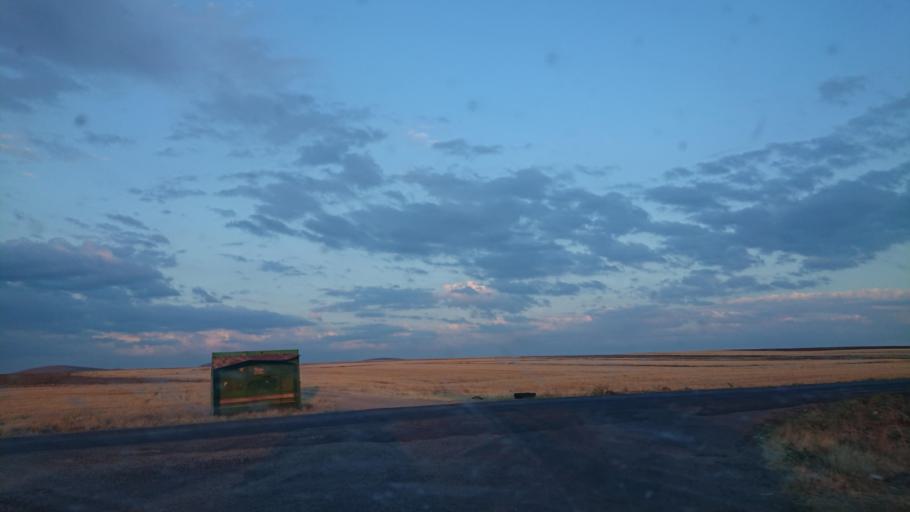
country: TR
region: Aksaray
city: Balci
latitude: 38.8273
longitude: 34.1373
